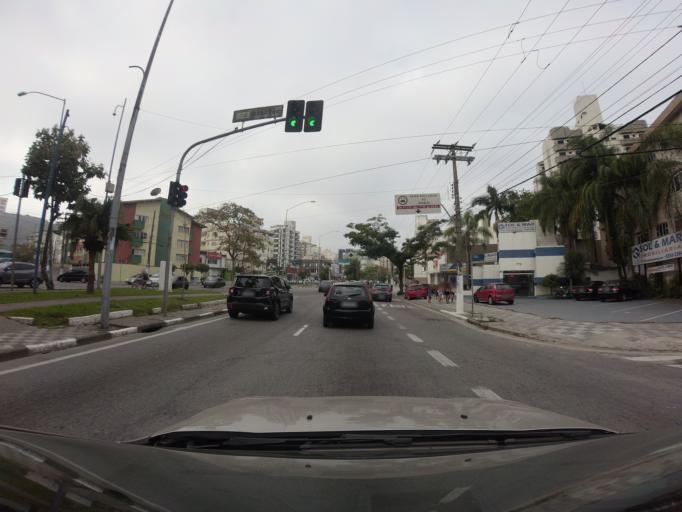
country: BR
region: Sao Paulo
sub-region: Guaruja
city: Guaruja
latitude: -23.9869
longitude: -46.2438
